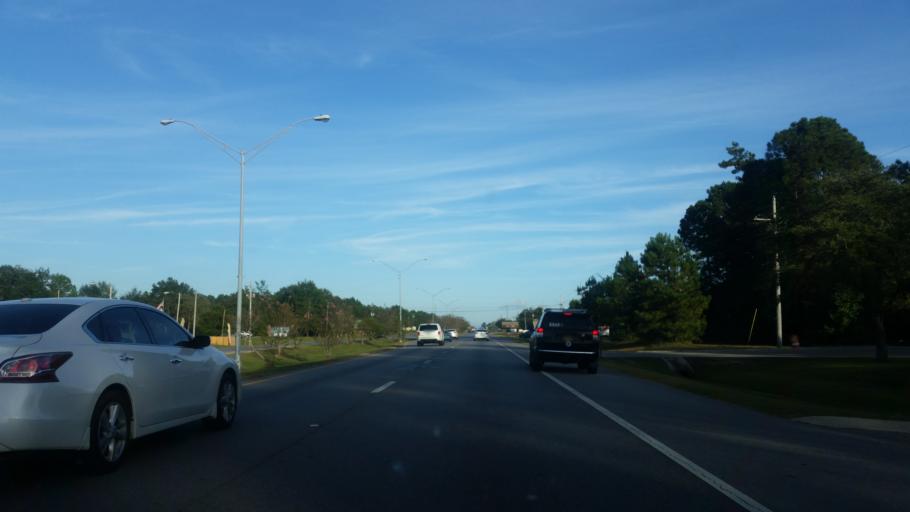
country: US
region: Mississippi
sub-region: Jackson County
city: Gulf Park Estates
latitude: 30.4109
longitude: -88.7720
